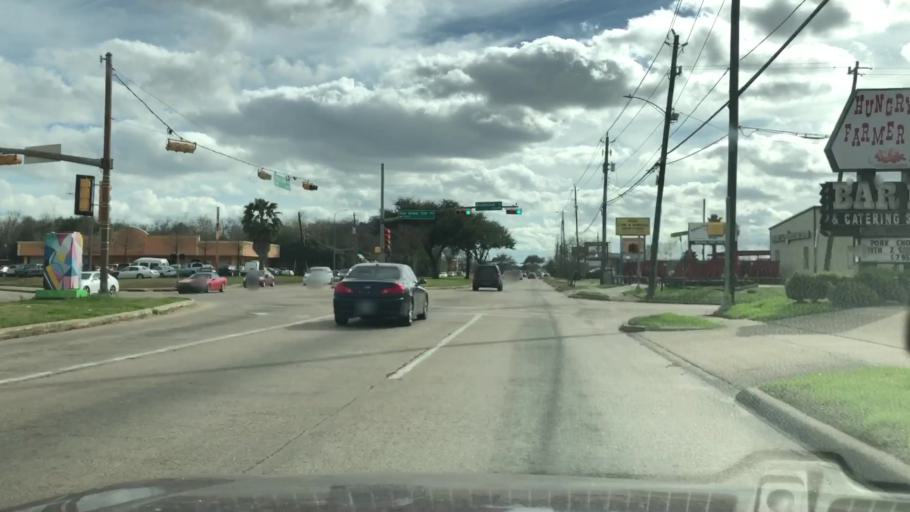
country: US
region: Texas
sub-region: Fort Bend County
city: Missouri City
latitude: 29.6153
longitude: -95.4650
